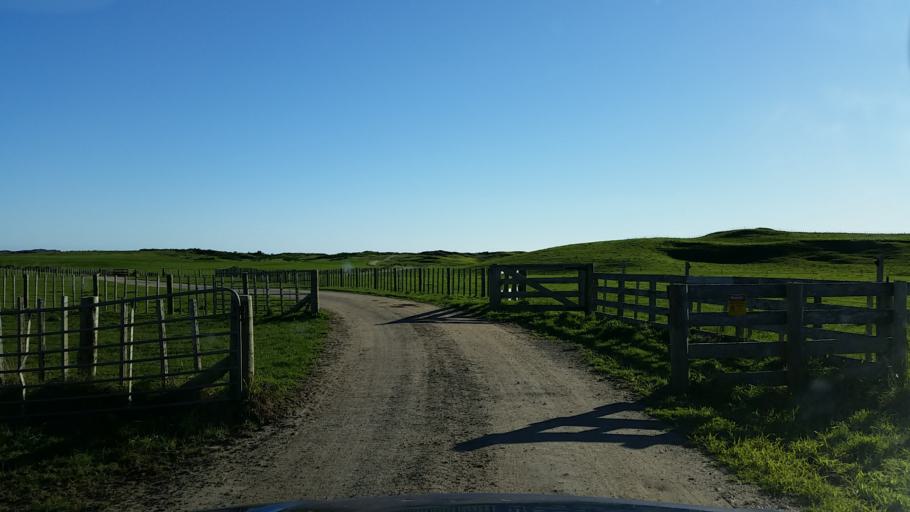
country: NZ
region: Taranaki
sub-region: South Taranaki District
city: Patea
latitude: -39.8369
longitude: 174.7002
